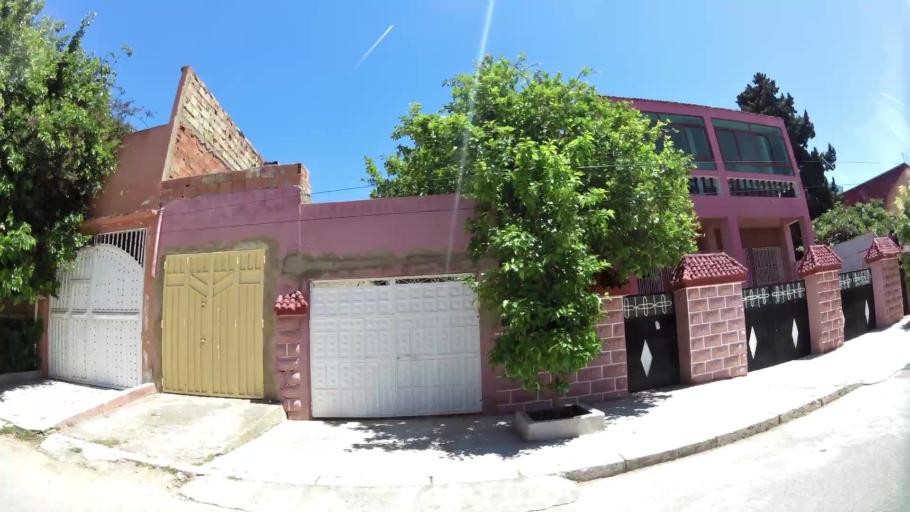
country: MA
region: Meknes-Tafilalet
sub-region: Meknes
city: Meknes
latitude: 33.9109
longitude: -5.5633
